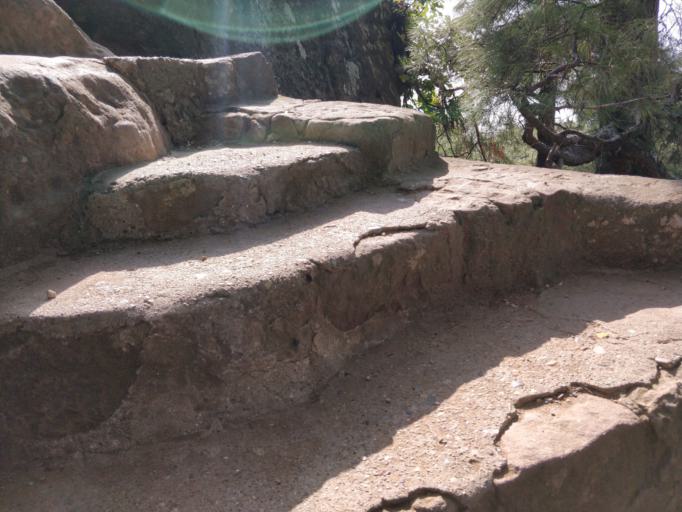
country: TR
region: Canakkale
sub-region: Merkez
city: Kucukkuyu
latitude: 39.5605
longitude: 26.6178
